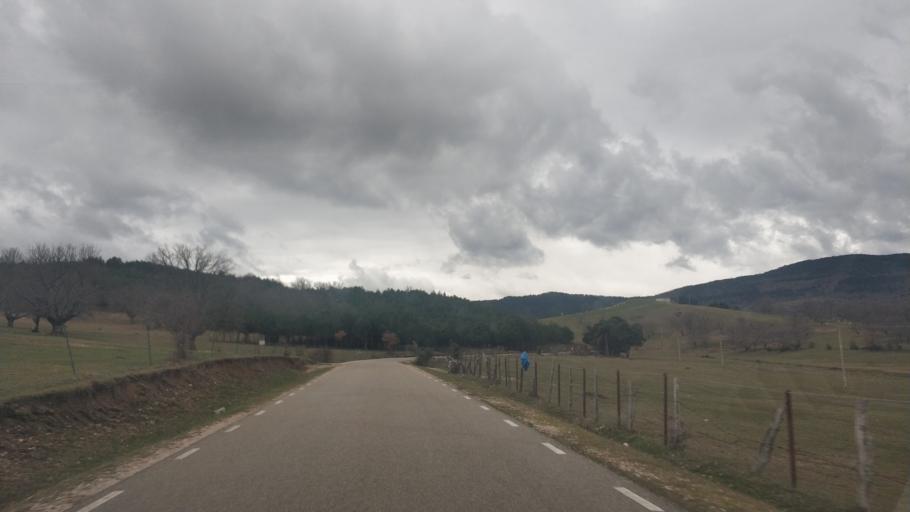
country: ES
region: Castille and Leon
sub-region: Provincia de Burgos
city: Canicosa de la Sierra
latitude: 41.9472
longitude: -3.0320
